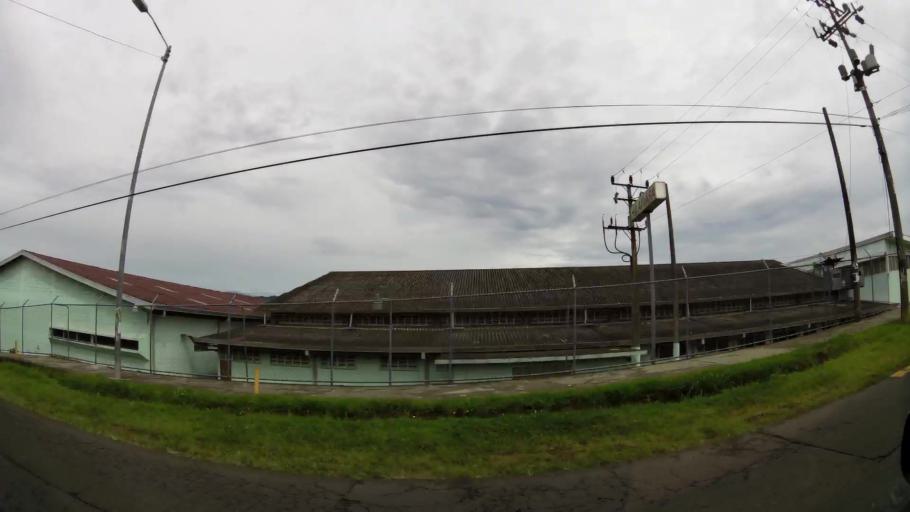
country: CR
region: San Jose
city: Ipis
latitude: 9.9647
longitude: -84.0119
